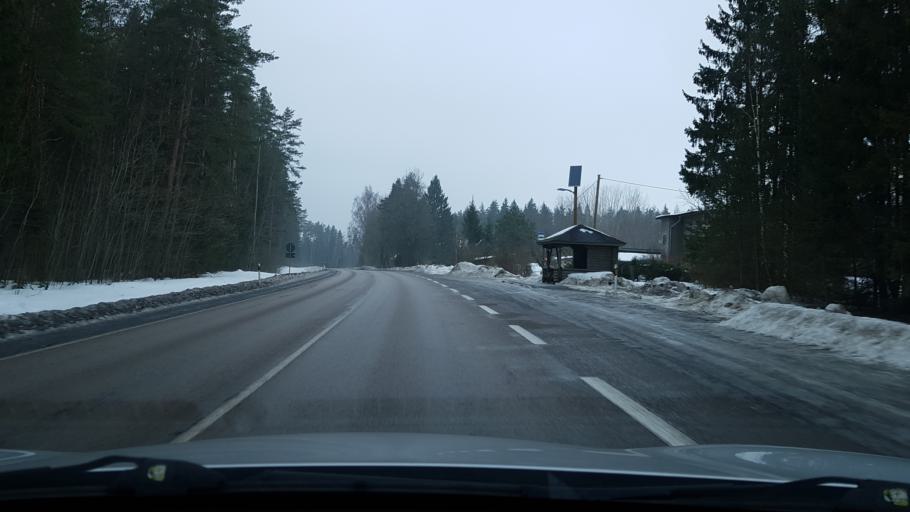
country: EE
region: Valgamaa
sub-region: Torva linn
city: Torva
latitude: 57.9878
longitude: 26.1737
